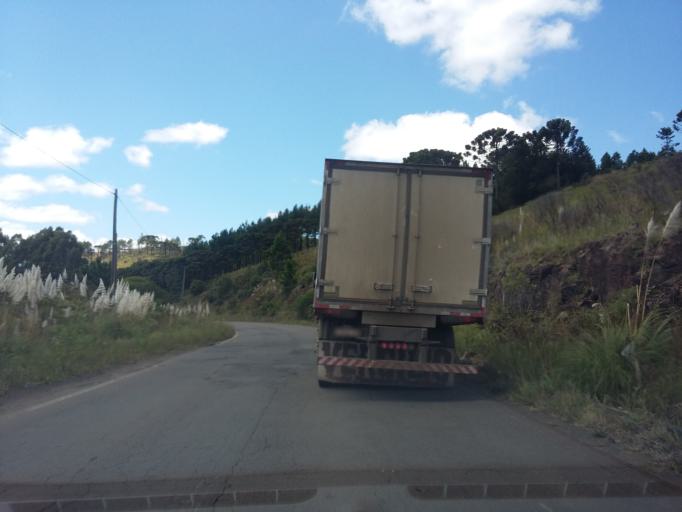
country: BR
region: Santa Catarina
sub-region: Sao Joaquim
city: Sao Joaquim
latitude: -28.2983
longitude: -49.7331
